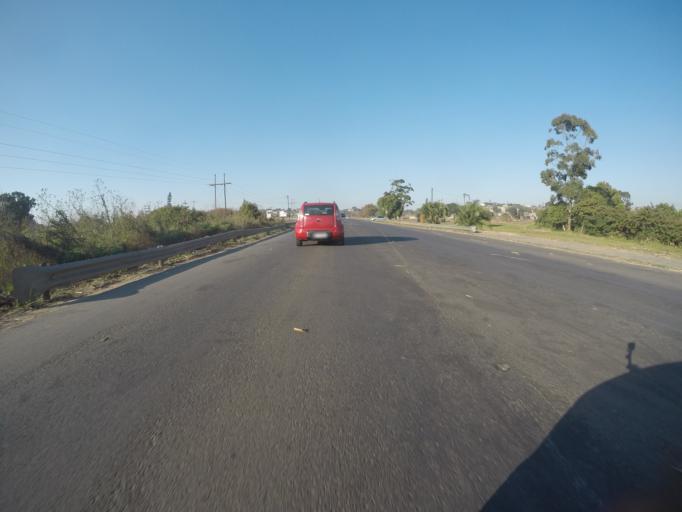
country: ZA
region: KwaZulu-Natal
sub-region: iLembe District Municipality
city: Stanger
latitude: -29.3971
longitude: 31.2519
